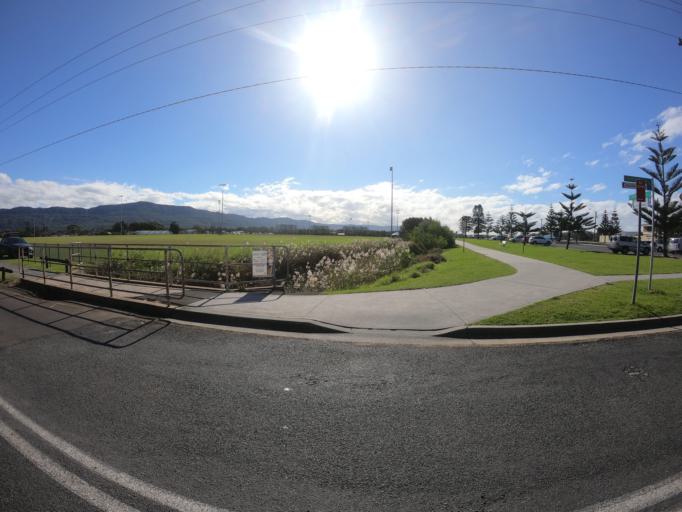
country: AU
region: New South Wales
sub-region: Wollongong
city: Fairy Meadow
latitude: -34.3968
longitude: 150.9040
